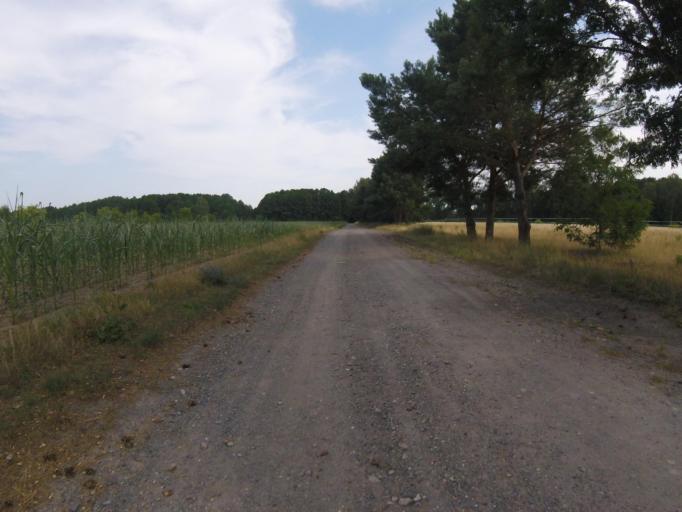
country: DE
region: Brandenburg
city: Erkner
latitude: 52.3114
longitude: 13.7536
